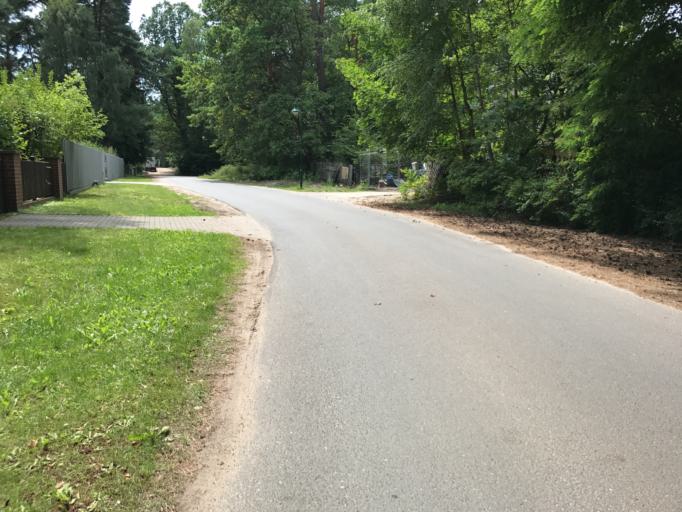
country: DE
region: Brandenburg
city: Wandlitz
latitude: 52.7566
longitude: 13.4358
